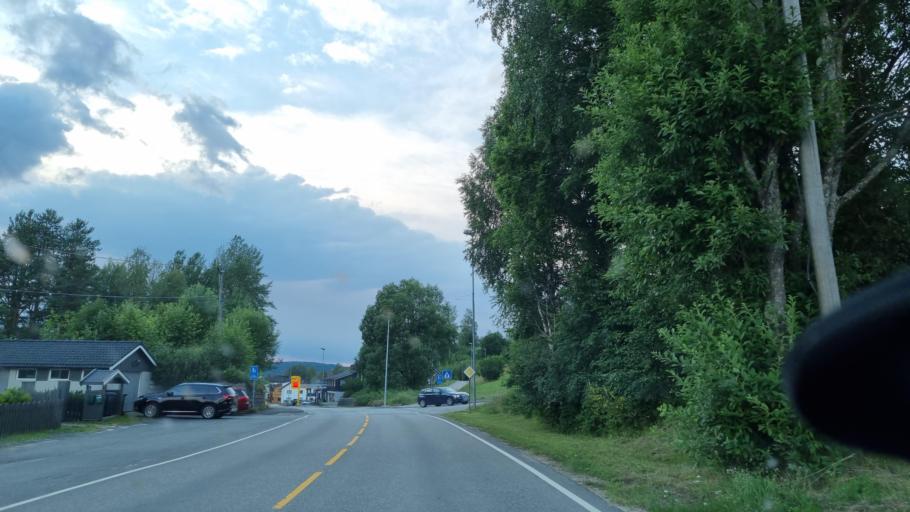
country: NO
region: Hedmark
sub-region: Trysil
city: Innbygda
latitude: 61.3103
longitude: 12.2715
